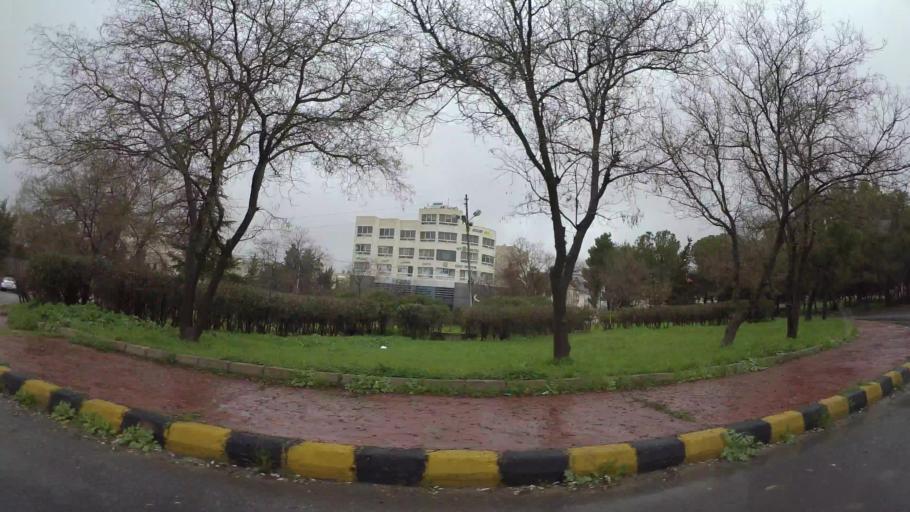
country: JO
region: Amman
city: Wadi as Sir
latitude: 31.9675
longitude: 35.8448
